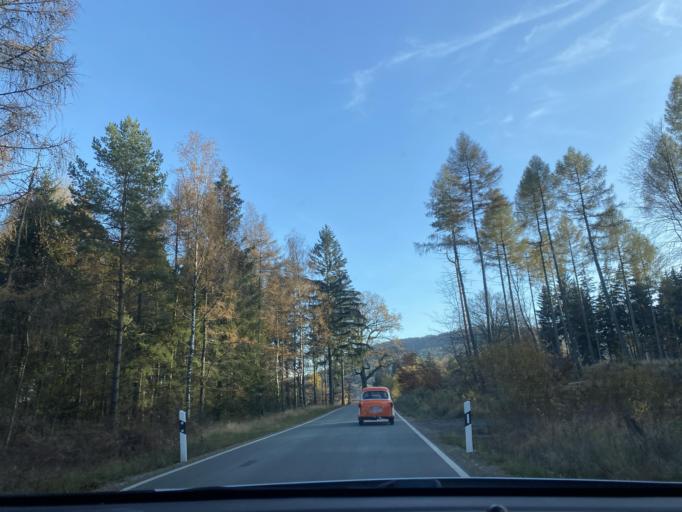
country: DE
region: Saxony
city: Kurort Oybin
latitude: 50.8391
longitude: 14.7210
